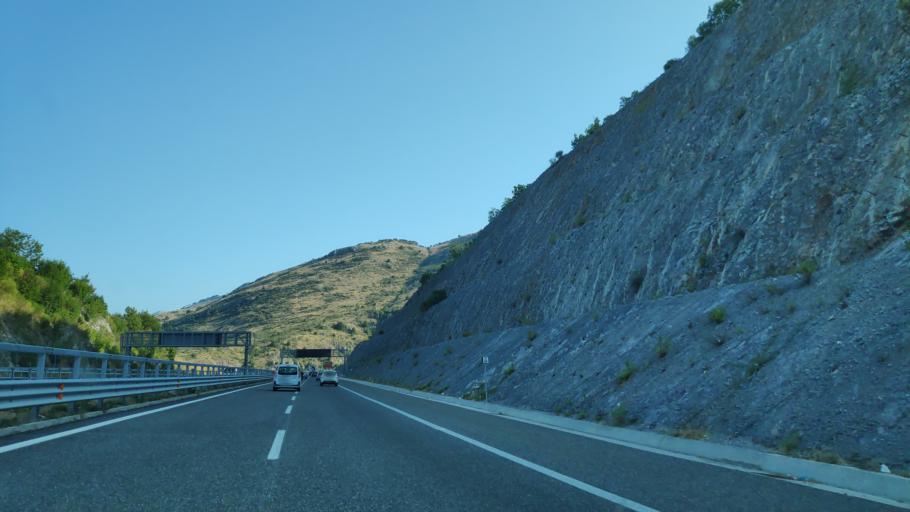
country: IT
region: Basilicate
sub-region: Provincia di Potenza
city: Lauria
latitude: 40.0303
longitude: 15.8748
